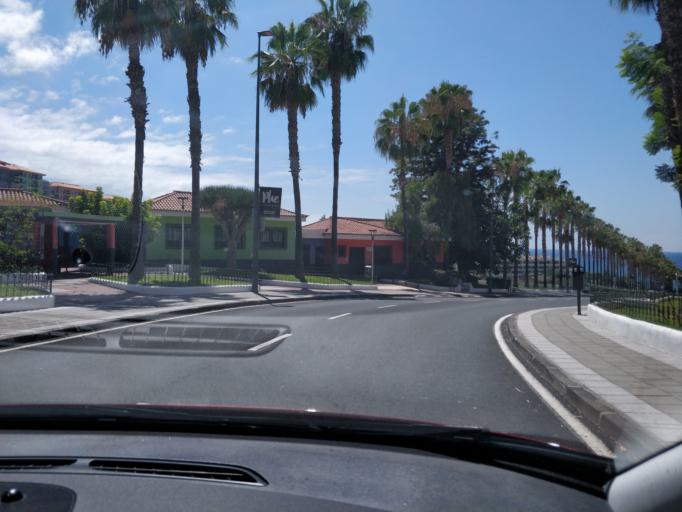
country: ES
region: Canary Islands
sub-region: Provincia de Santa Cruz de Tenerife
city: Puerto de la Cruz
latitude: 28.4102
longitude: -16.5541
